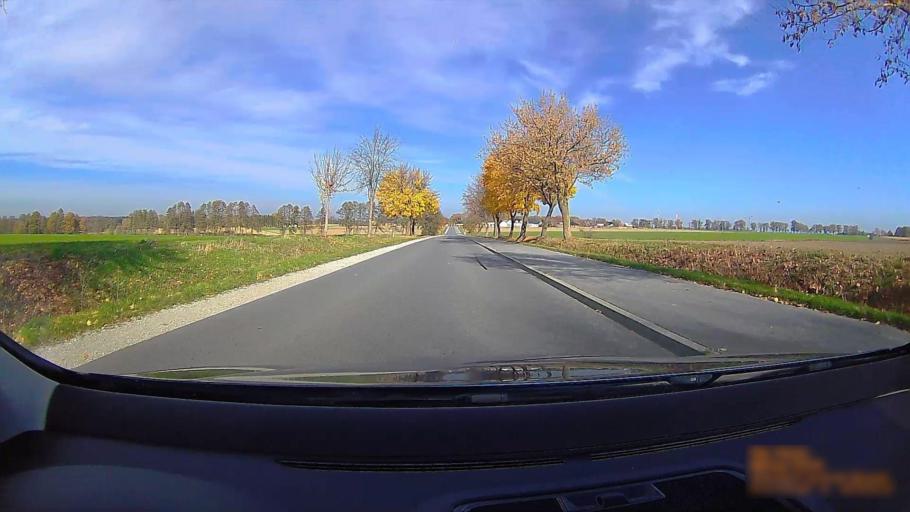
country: PL
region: Greater Poland Voivodeship
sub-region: Powiat ostrzeszowski
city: Doruchow
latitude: 51.3519
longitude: 18.0273
